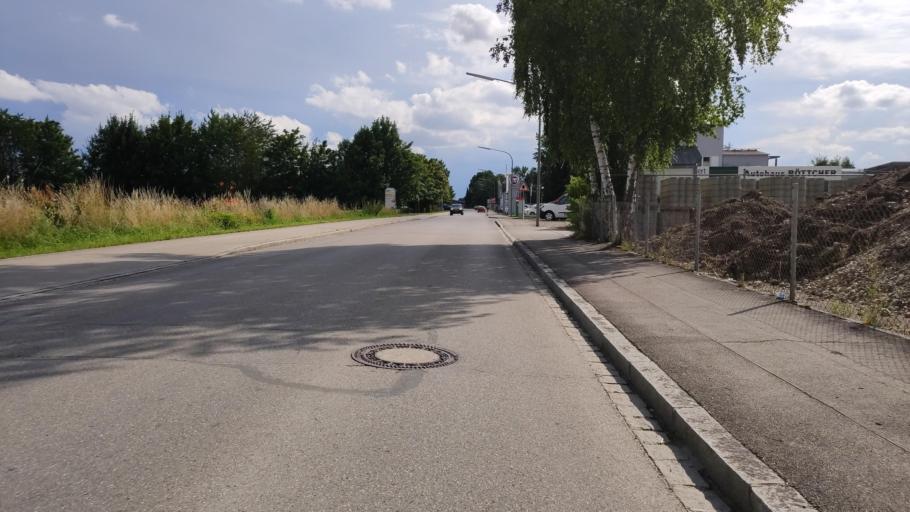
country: DE
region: Bavaria
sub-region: Swabia
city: Bobingen
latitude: 48.2671
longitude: 10.8442
